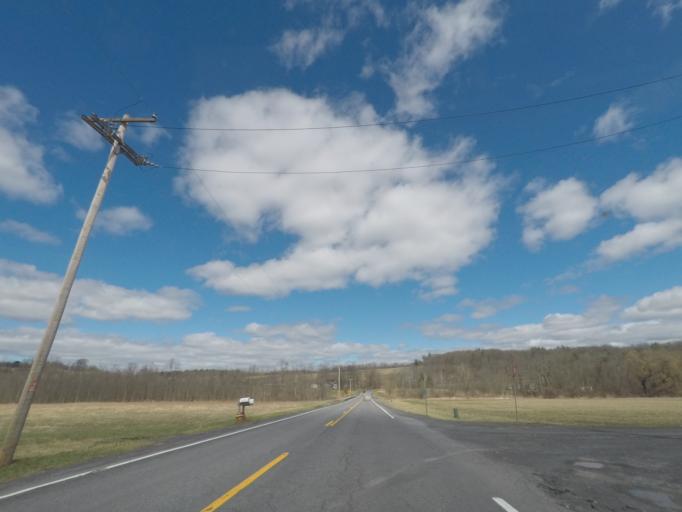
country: US
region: New York
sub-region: Albany County
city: Voorheesville
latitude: 42.5707
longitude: -73.9204
